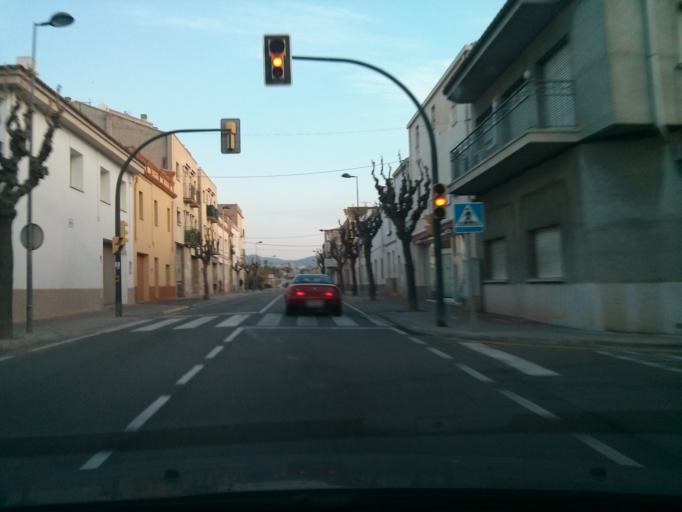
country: ES
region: Catalonia
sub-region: Provincia de Tarragona
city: Sant Jaume dels Domenys
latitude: 41.2821
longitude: 1.5538
